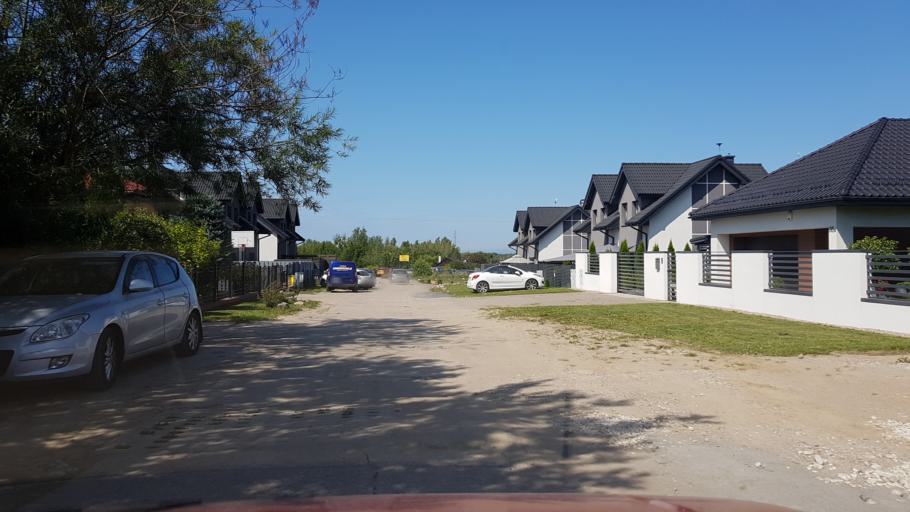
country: PL
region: West Pomeranian Voivodeship
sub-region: Koszalin
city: Koszalin
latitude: 54.2217
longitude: 16.1675
